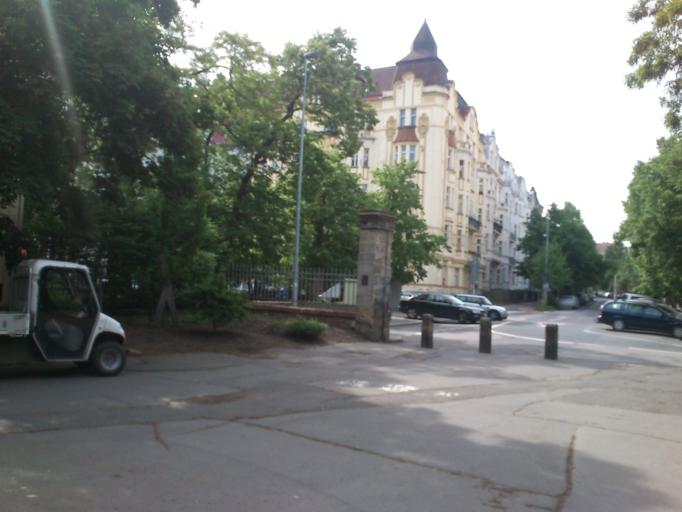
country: CZ
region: Praha
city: Prague
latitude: 50.1031
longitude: 14.4226
